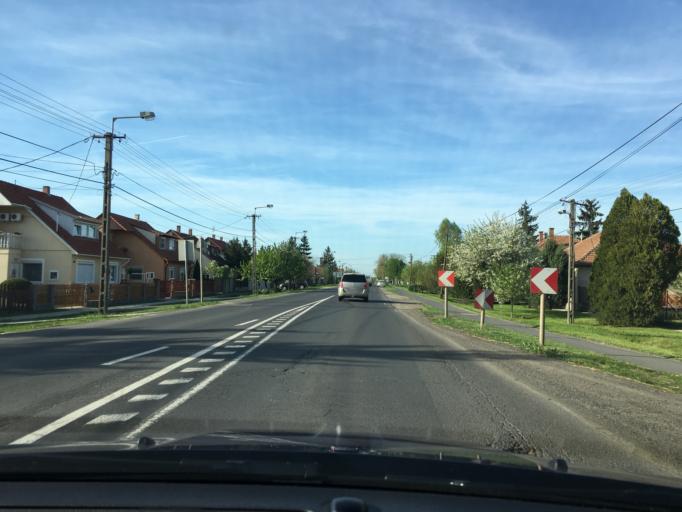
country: HU
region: Bekes
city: Mezobereny
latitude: 46.8355
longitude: 21.0275
